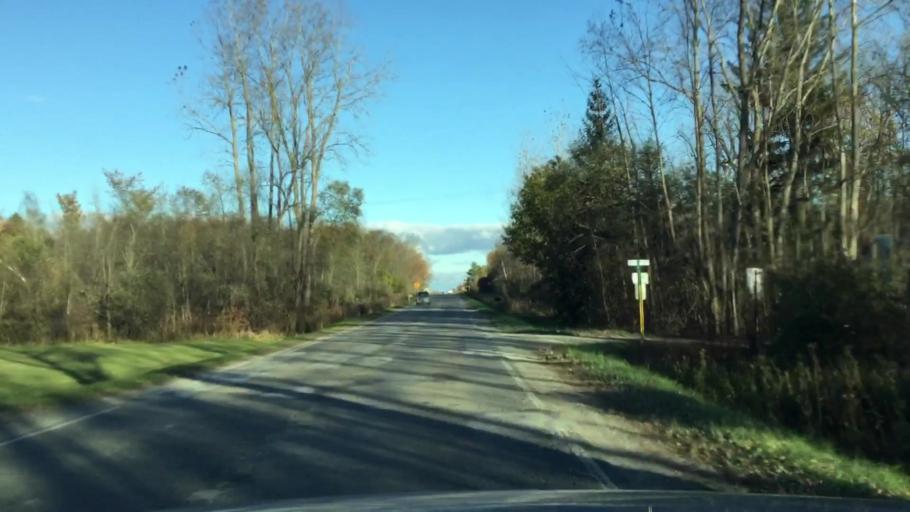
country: US
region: Michigan
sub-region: Lapeer County
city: Imlay City
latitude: 43.0624
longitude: -83.1742
